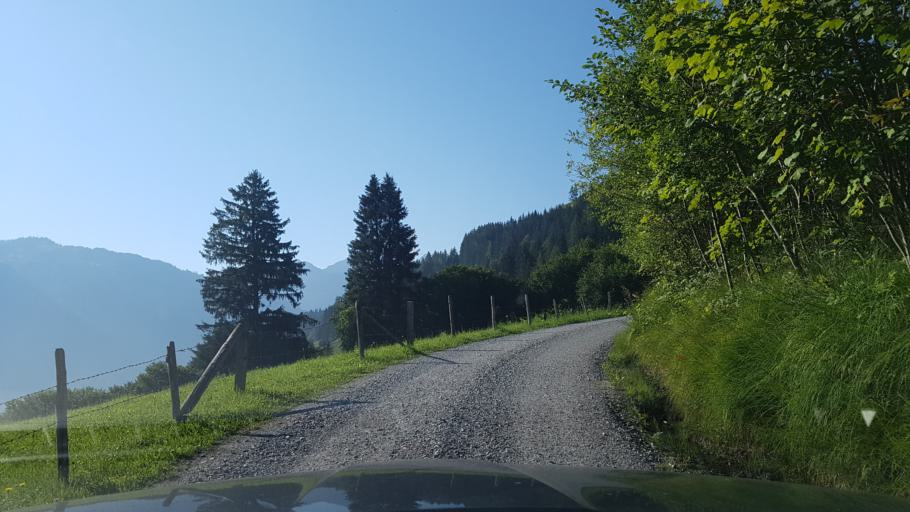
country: AT
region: Salzburg
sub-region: Politischer Bezirk Sankt Johann im Pongau
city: Dorfgastein
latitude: 47.2567
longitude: 13.0779
